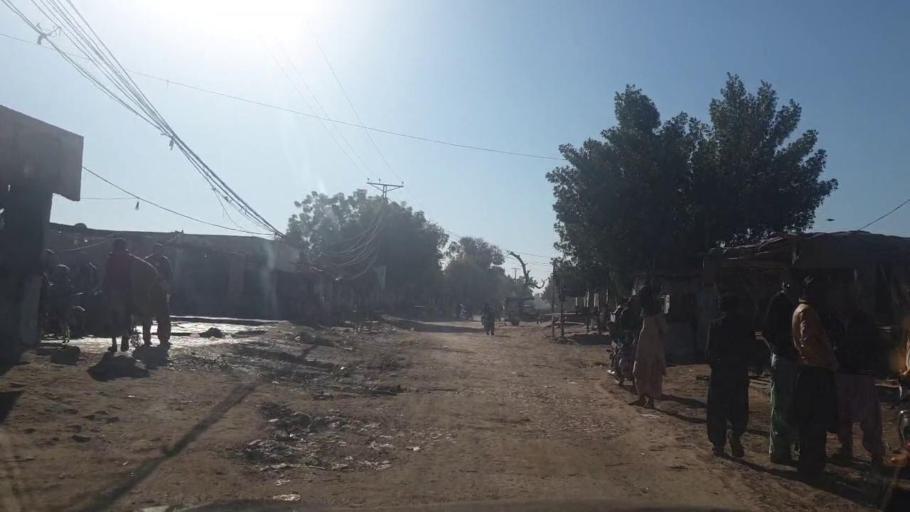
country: PK
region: Sindh
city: Ghotki
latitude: 27.9927
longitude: 69.3163
